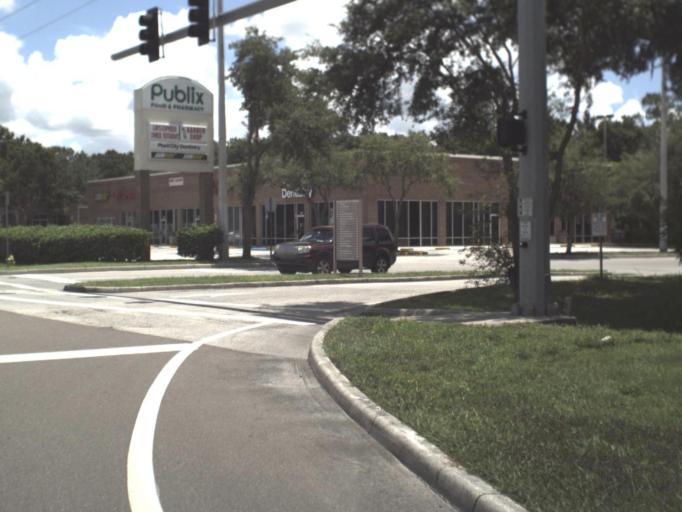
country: US
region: Florida
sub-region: Hillsborough County
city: Plant City
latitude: 28.0243
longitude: -82.1482
